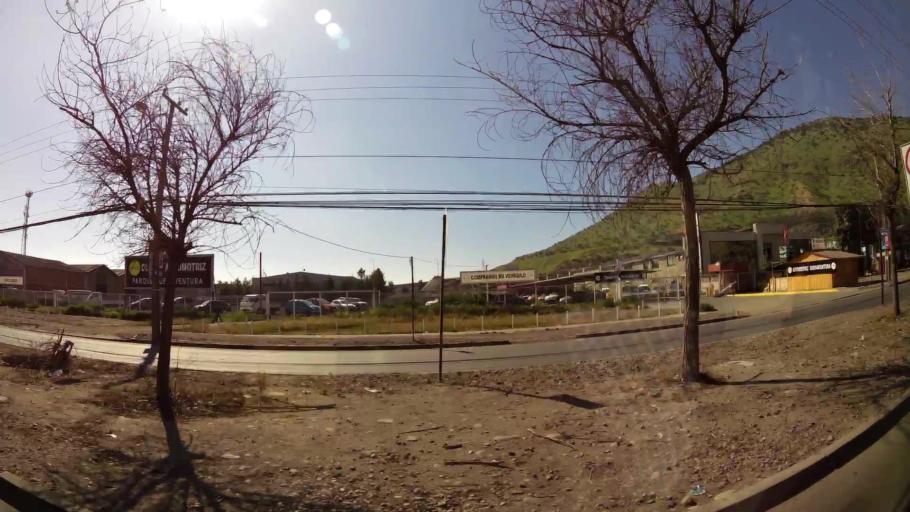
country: CL
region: Santiago Metropolitan
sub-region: Provincia de Chacabuco
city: Chicureo Abajo
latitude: -33.3305
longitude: -70.7030
